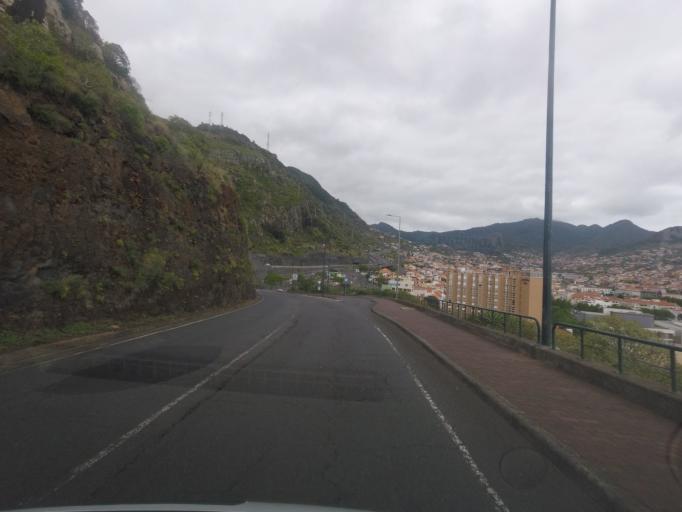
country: PT
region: Madeira
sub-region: Machico
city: Machico
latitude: 32.7137
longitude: -16.7644
